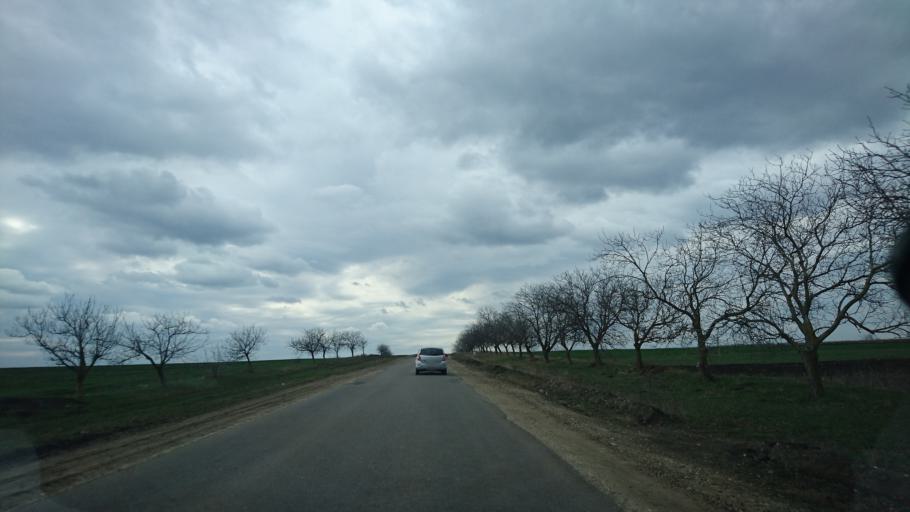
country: MD
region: Gagauzia
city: Comrat
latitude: 46.3080
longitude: 28.6101
